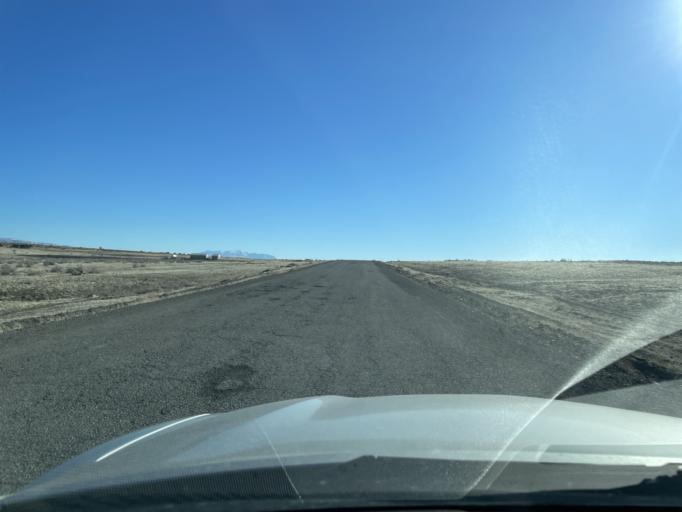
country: US
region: Colorado
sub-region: Mesa County
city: Loma
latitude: 39.1810
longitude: -109.1300
